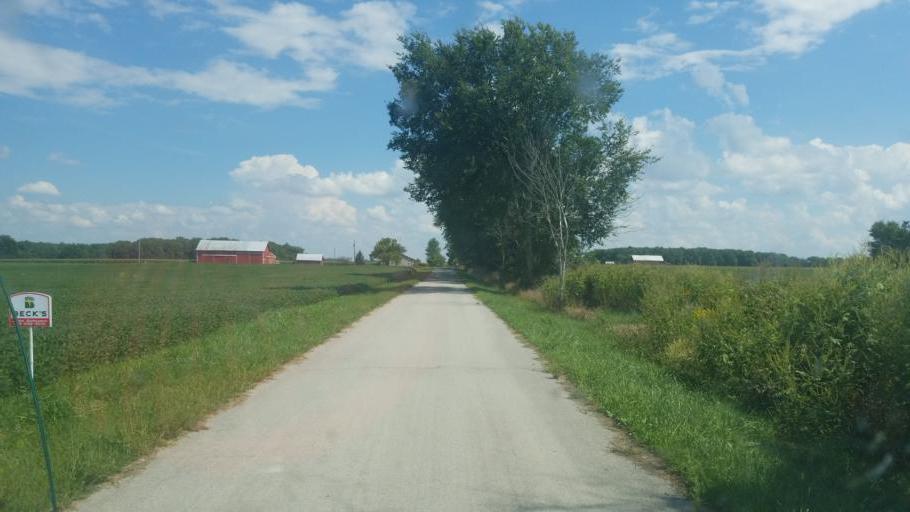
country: US
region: Ohio
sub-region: Hardin County
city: Forest
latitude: 40.8468
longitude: -83.4219
